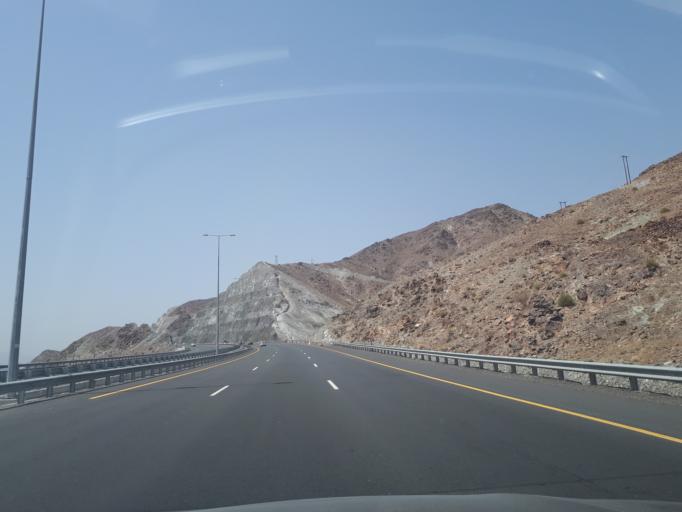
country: OM
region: Muhafazat ad Dakhiliyah
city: Bidbid
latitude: 23.3754
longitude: 58.1029
